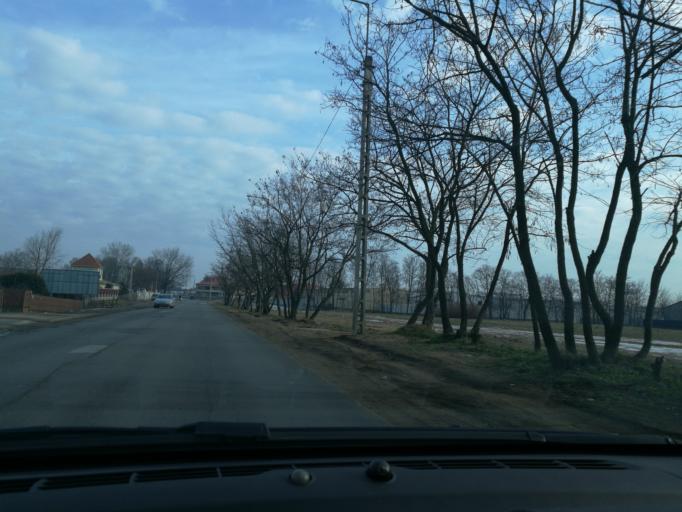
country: HU
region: Szabolcs-Szatmar-Bereg
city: Nyiregyhaza
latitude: 47.9334
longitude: 21.7355
